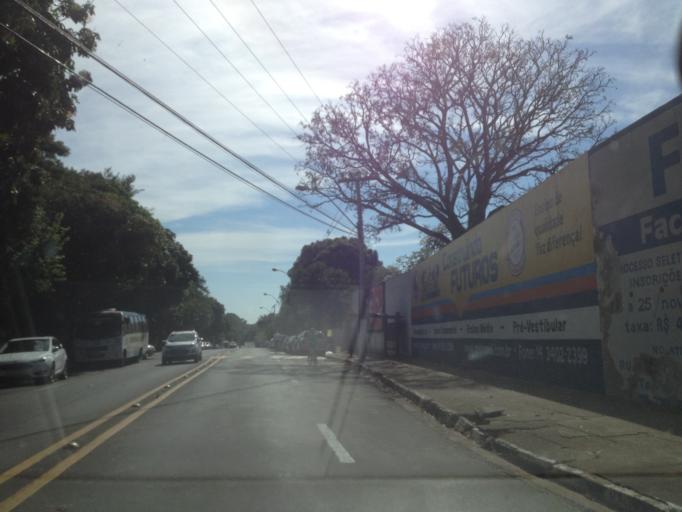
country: BR
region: Sao Paulo
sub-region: Marilia
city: Marilia
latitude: -22.2061
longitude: -49.9342
